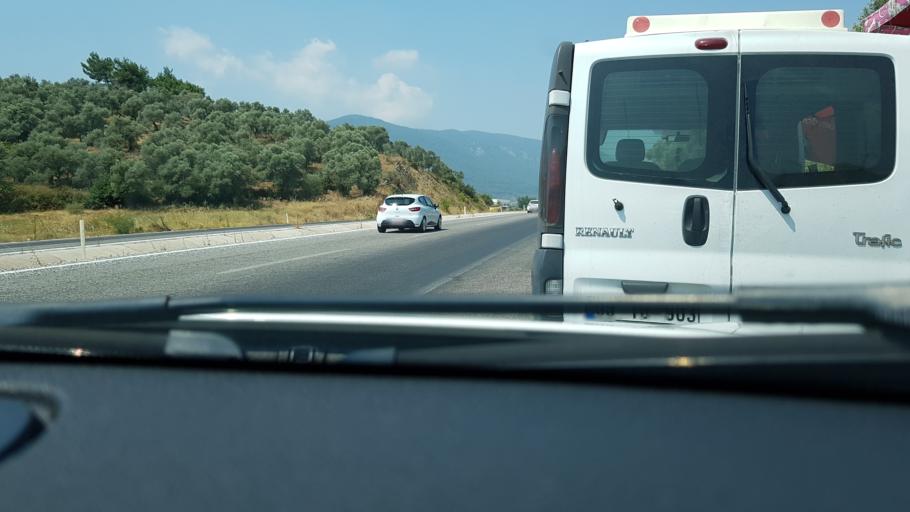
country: TR
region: Mugla
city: Selimiye
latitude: 37.4114
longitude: 27.6317
